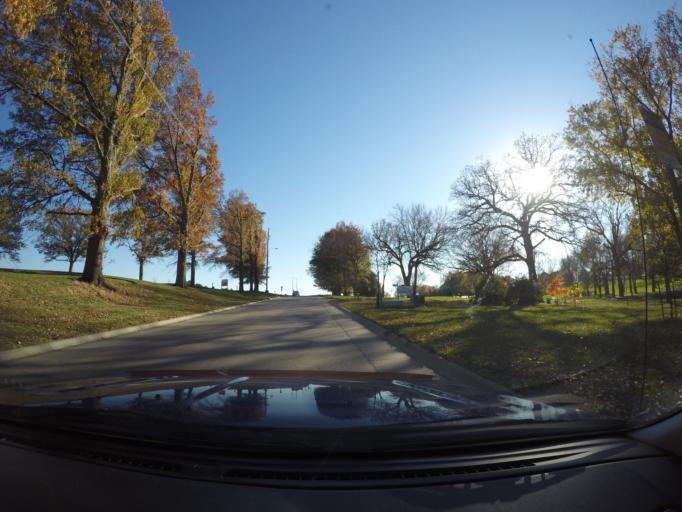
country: US
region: Nebraska
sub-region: Otoe County
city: Nebraska City
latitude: 40.6719
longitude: -95.8783
